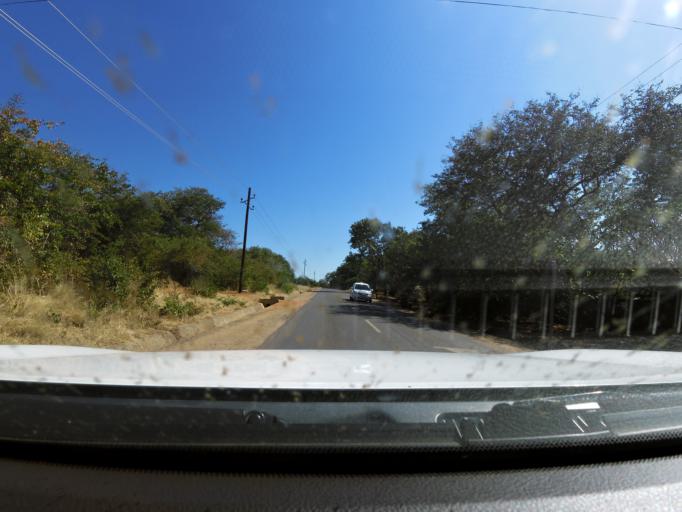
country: ZW
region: Matabeleland North
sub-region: Hwange District
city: Victoria Falls
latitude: -17.9279
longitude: 25.8281
